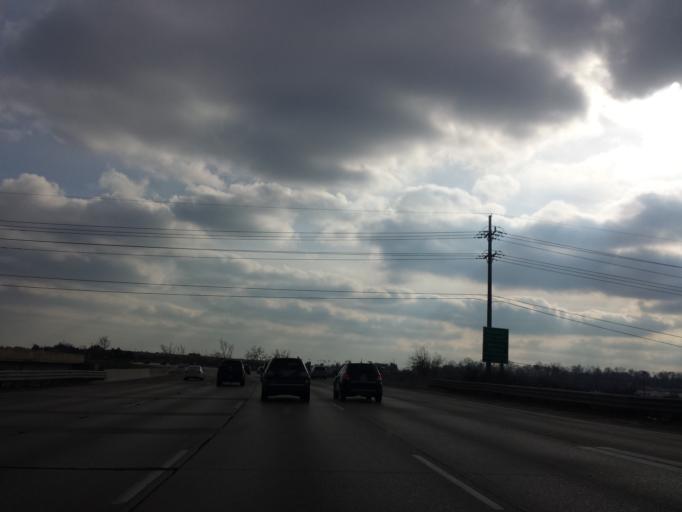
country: US
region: Michigan
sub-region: Wayne County
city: Northville
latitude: 42.4397
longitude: -83.4325
